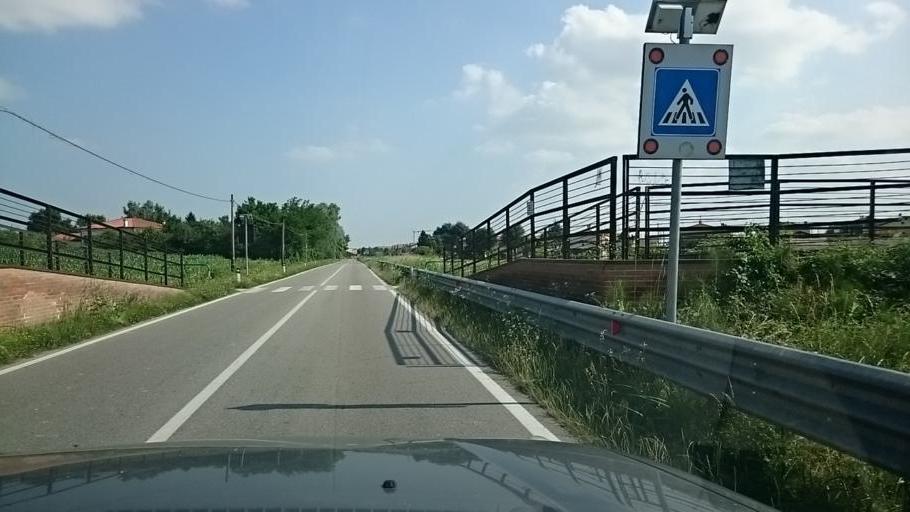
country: IT
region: Veneto
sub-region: Provincia di Padova
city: San Giorgio delle Pertiche
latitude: 45.5503
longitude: 11.8732
